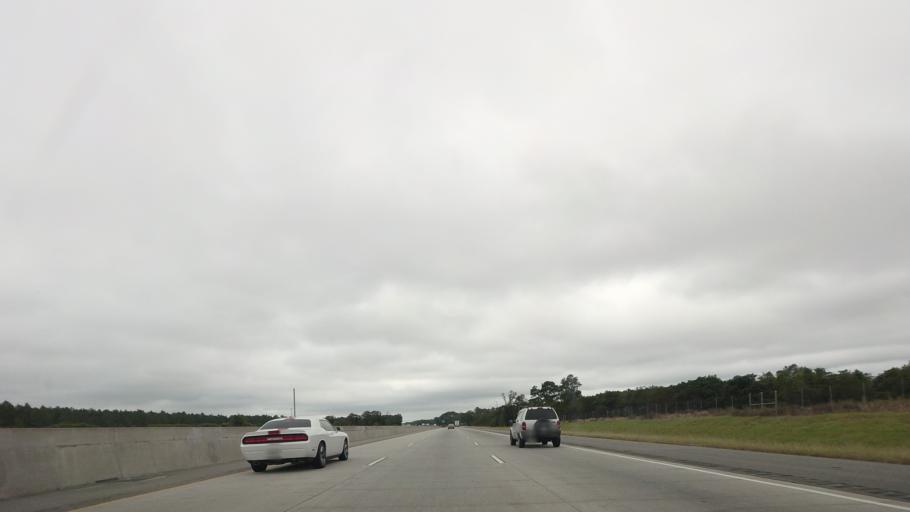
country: US
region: Georgia
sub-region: Tift County
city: Omega
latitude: 31.2931
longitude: -83.4771
